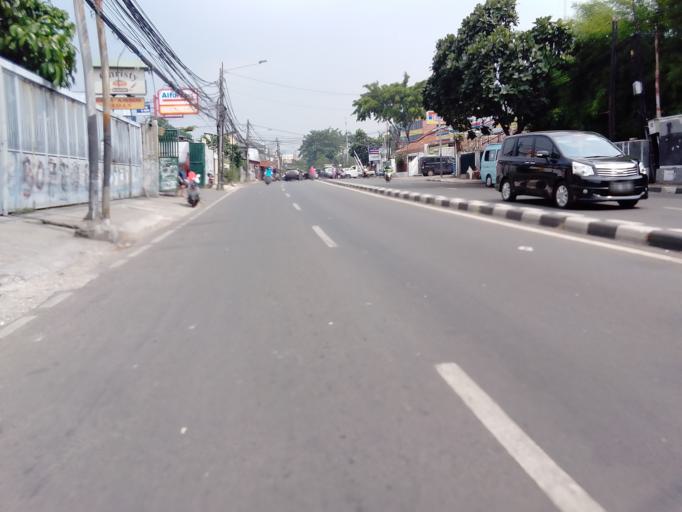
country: ID
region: Jakarta Raya
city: Jakarta
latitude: -6.1911
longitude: 106.8063
